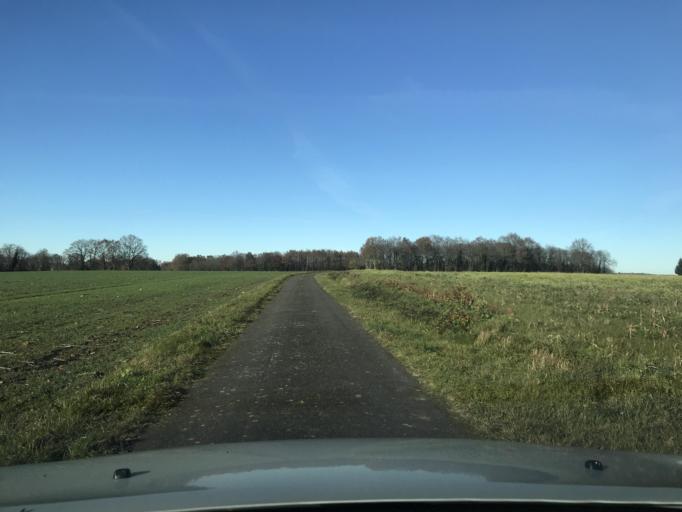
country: FR
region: Poitou-Charentes
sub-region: Departement de la Charente
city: Saint-Claud
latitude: 45.8584
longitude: 0.4956
